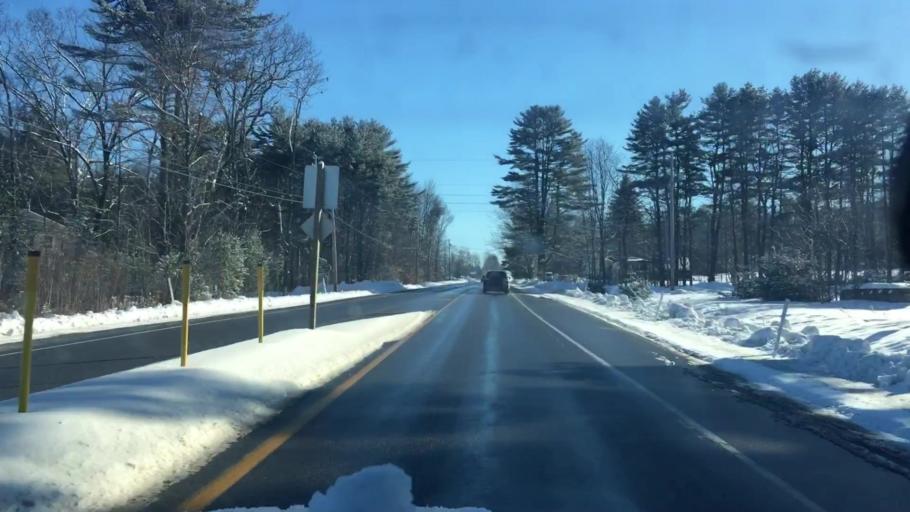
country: US
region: Maine
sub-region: Cumberland County
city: Bridgton
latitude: 44.0240
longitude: -70.6902
